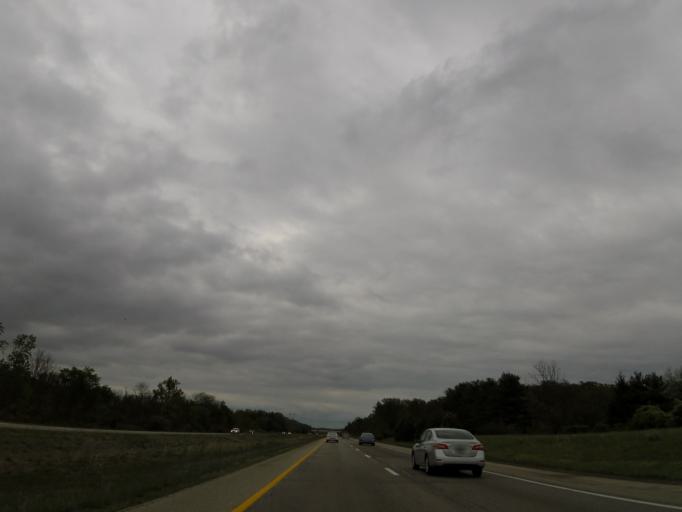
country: US
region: Ohio
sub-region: Madison County
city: Mount Sterling
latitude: 39.8075
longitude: -83.1992
